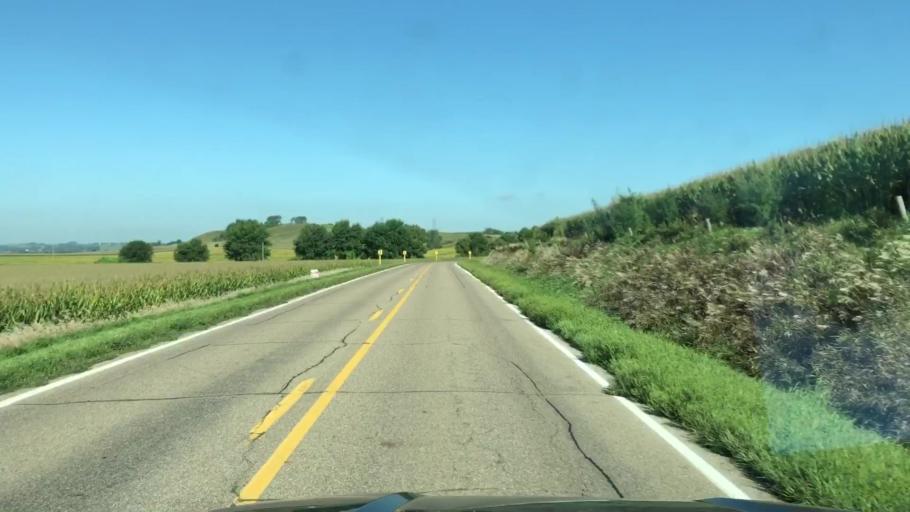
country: US
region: Iowa
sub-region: Woodbury County
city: Sergeant Bluff
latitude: 42.4080
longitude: -96.2542
